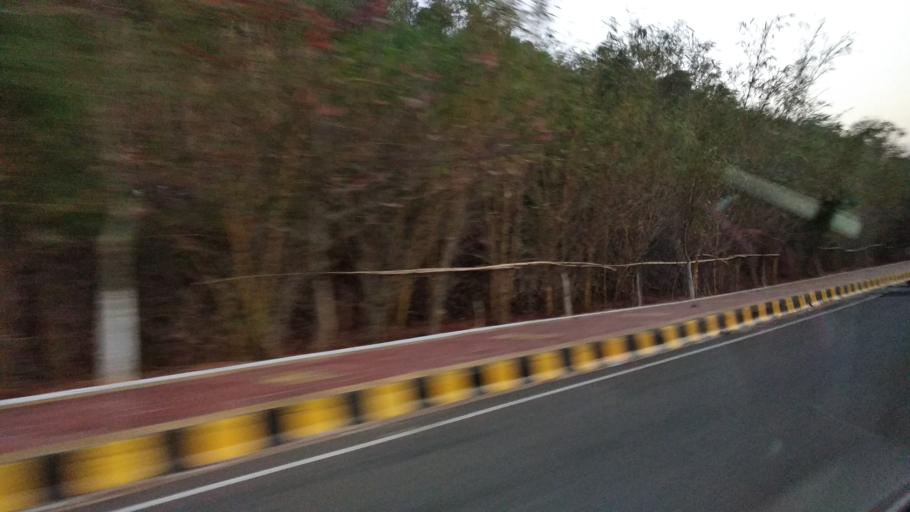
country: IN
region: Andhra Pradesh
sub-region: Vishakhapatnam
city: Bhimunipatnam
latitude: 17.7802
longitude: 83.3801
